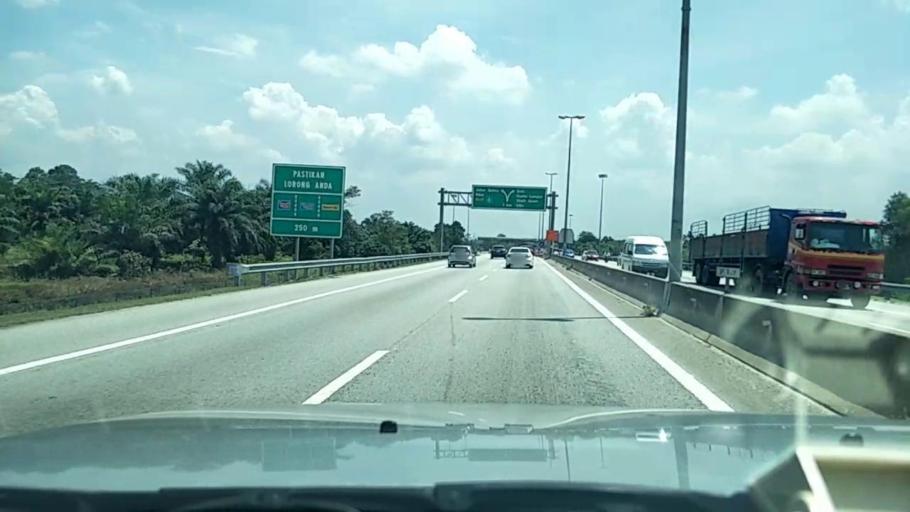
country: MY
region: Putrajaya
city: Putrajaya
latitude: 2.9265
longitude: 101.6167
